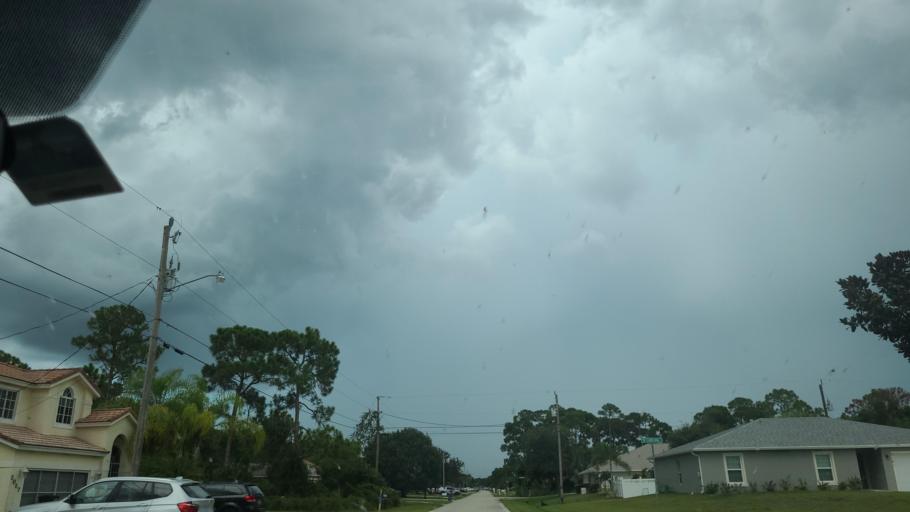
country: US
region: Florida
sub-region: Saint Lucie County
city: Port Saint Lucie
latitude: 27.2529
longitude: -80.4122
